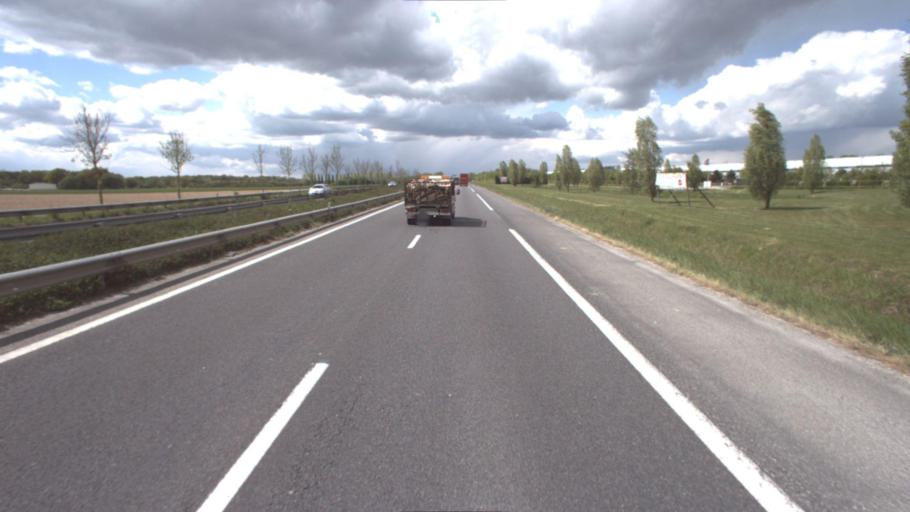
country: FR
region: Ile-de-France
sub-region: Departement de Seine-et-Marne
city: Neufmoutiers-en-Brie
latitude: 48.7252
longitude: 2.8244
